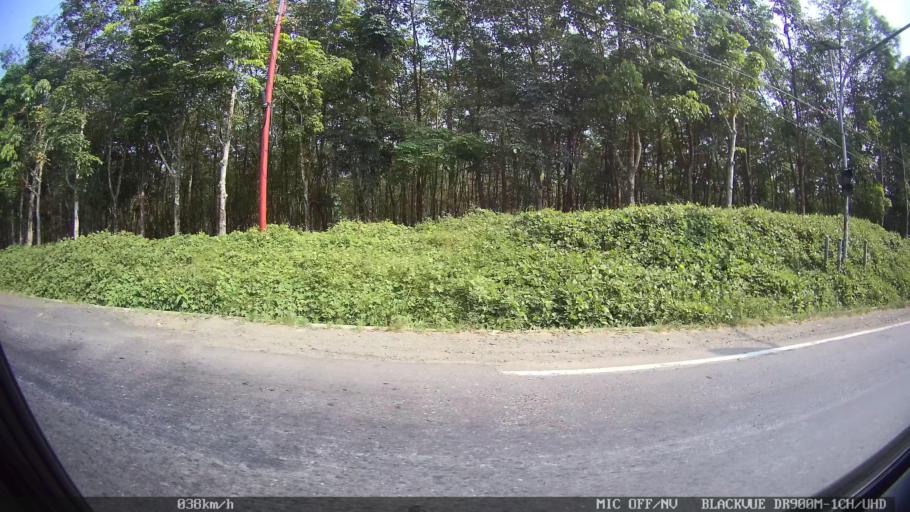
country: ID
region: Lampung
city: Gedongtataan
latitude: -5.3686
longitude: 105.1370
